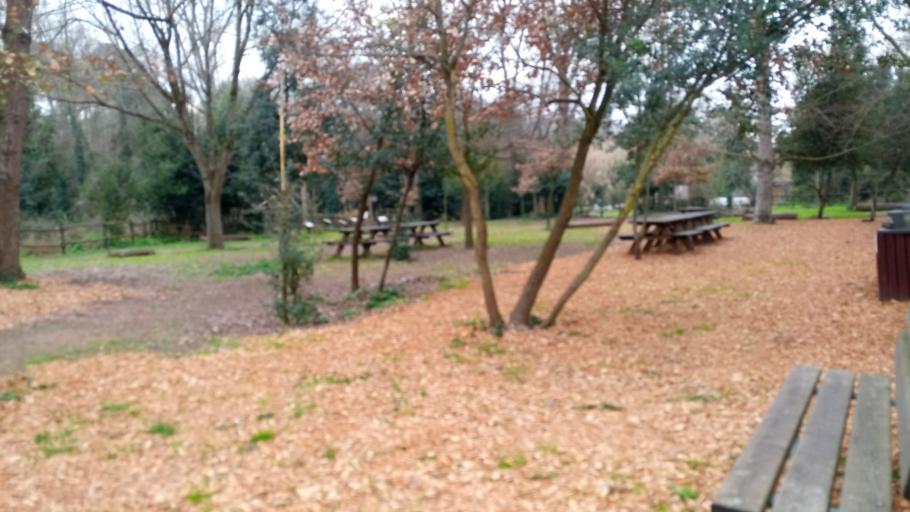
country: IT
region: Latium
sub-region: Citta metropolitana di Roma Capitale
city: Rome
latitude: 41.8678
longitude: 12.5013
